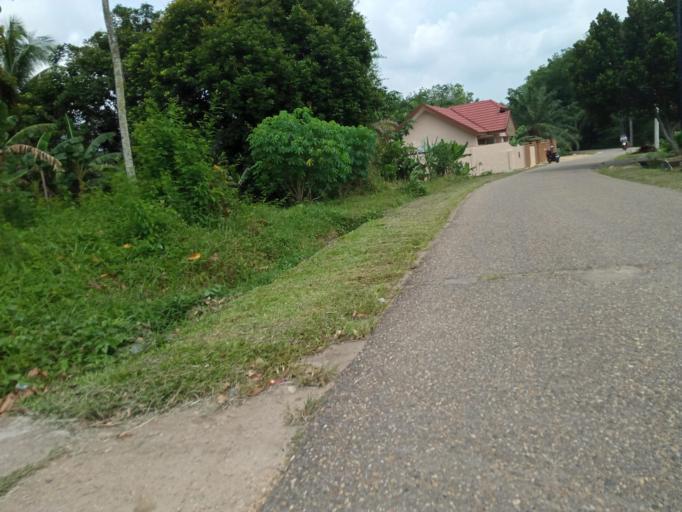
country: ID
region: Jambi
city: Muara Bulian
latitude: -1.7101
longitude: 103.2599
